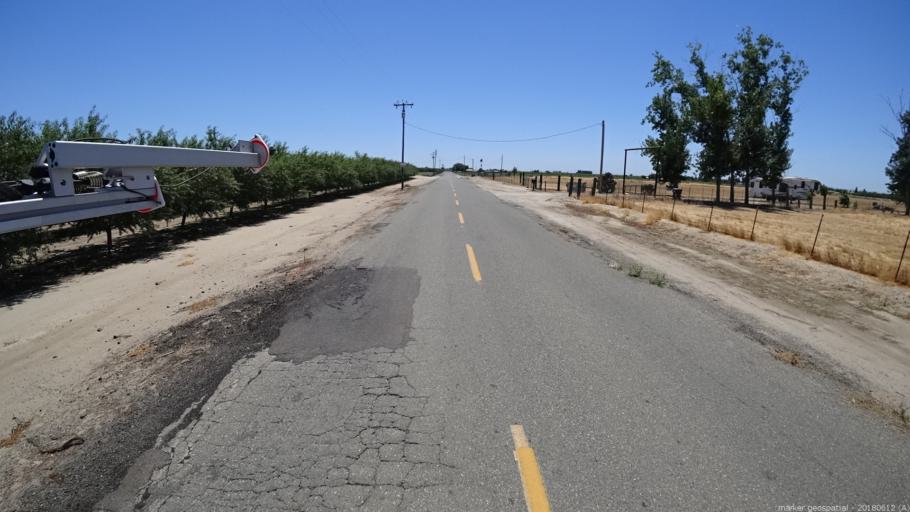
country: US
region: California
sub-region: Madera County
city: Chowchilla
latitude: 37.0954
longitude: -120.2746
